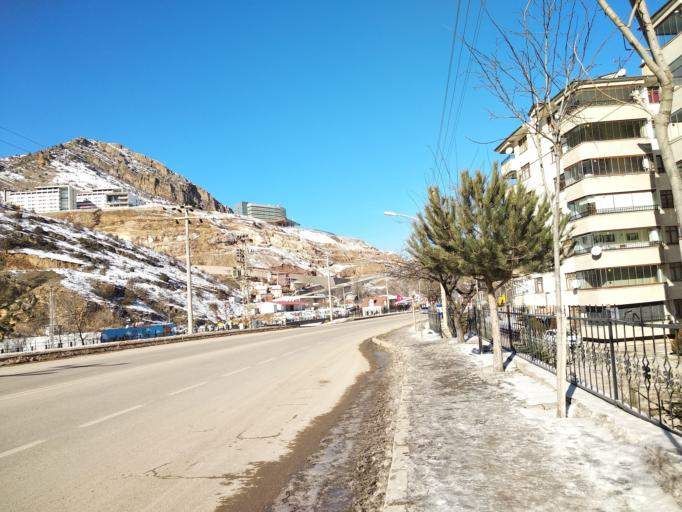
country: TR
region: Gumushane
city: Gumushkhane
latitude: 40.4382
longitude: 39.5050
